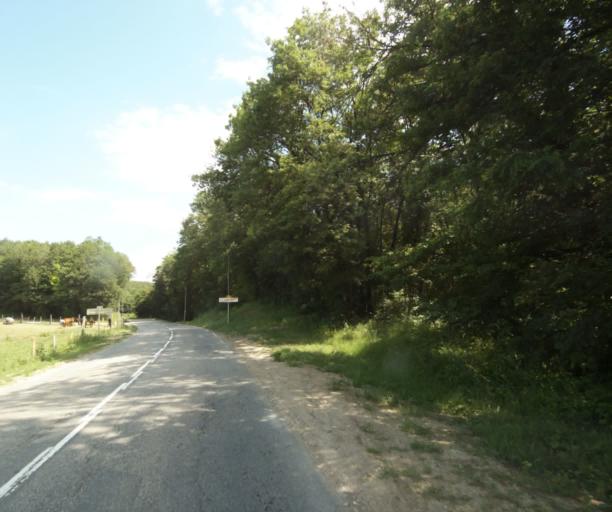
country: FR
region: Rhone-Alpes
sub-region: Departement de la Haute-Savoie
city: Armoy
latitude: 46.3561
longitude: 6.5146
